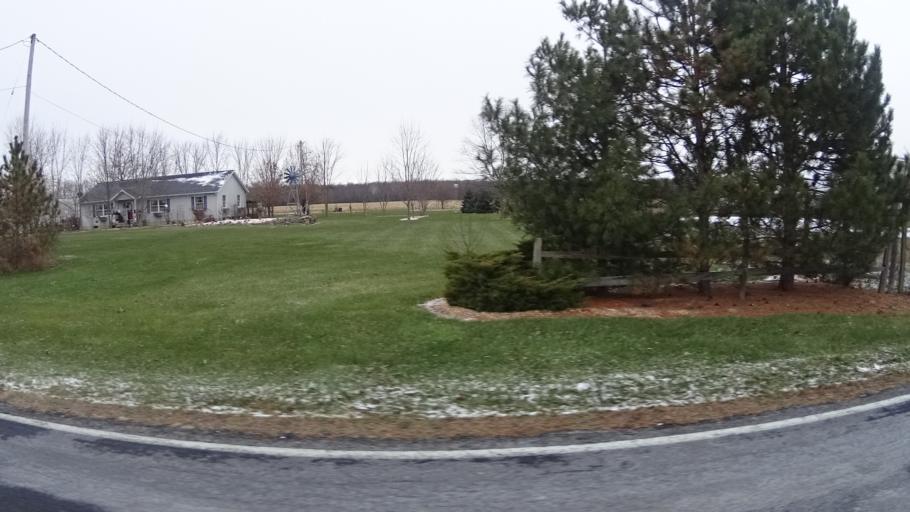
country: US
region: Ohio
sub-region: Lorain County
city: Lagrange
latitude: 41.2119
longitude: -82.1580
